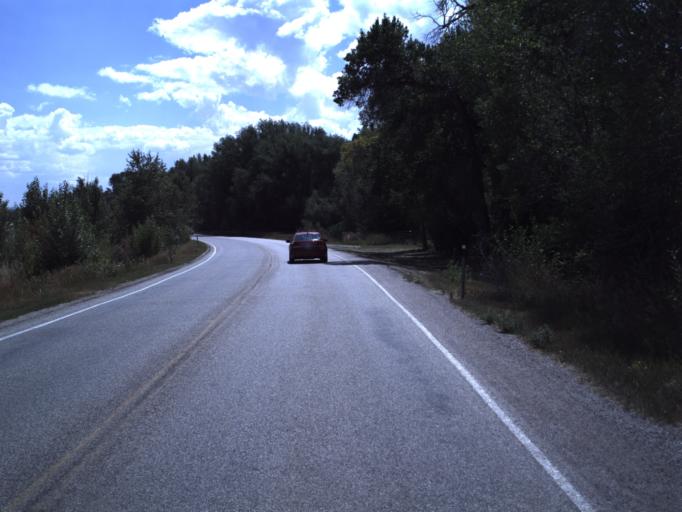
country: US
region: Idaho
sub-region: Bear Lake County
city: Paris
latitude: 41.9716
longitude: -111.4026
